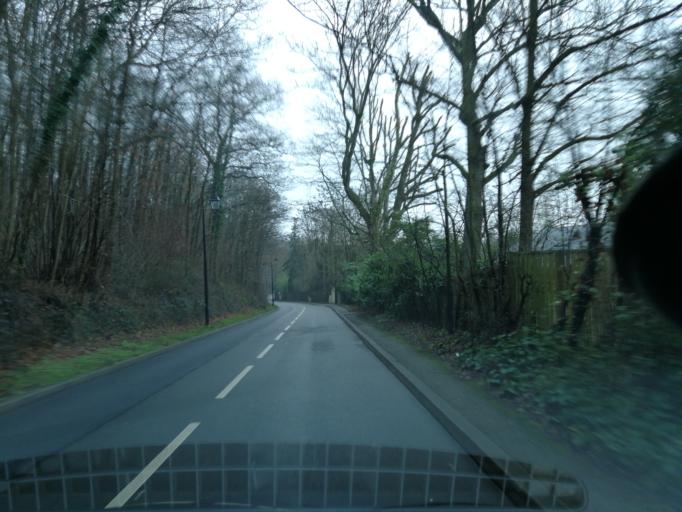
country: FR
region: Ile-de-France
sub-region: Departement des Yvelines
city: Buc
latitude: 48.7745
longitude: 2.1362
